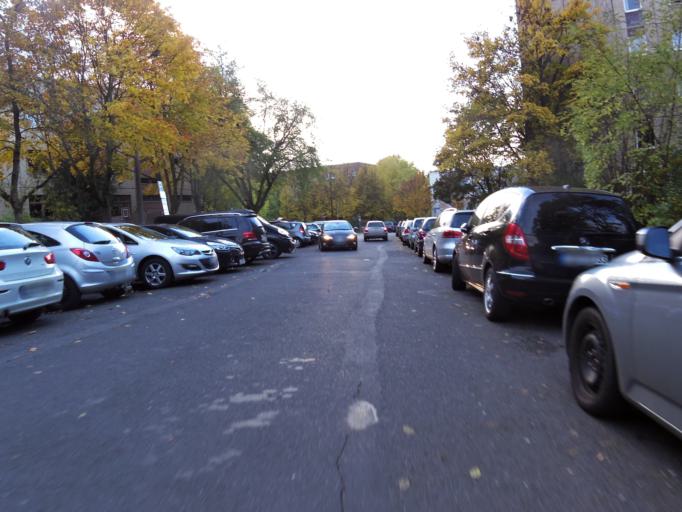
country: DE
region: Saxony
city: Leipzig
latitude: 51.3366
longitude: 12.3694
